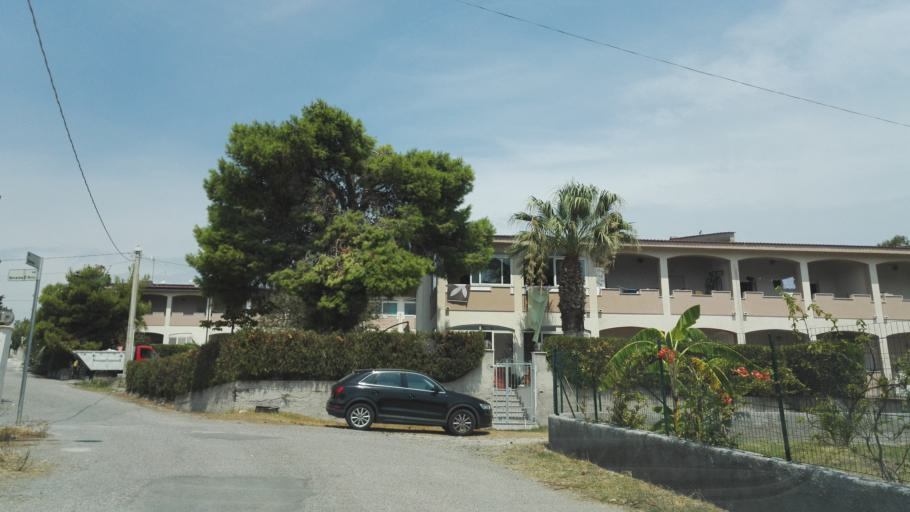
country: IT
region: Calabria
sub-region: Provincia di Reggio Calabria
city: Riace Marina
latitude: 38.3910
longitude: 16.5260
